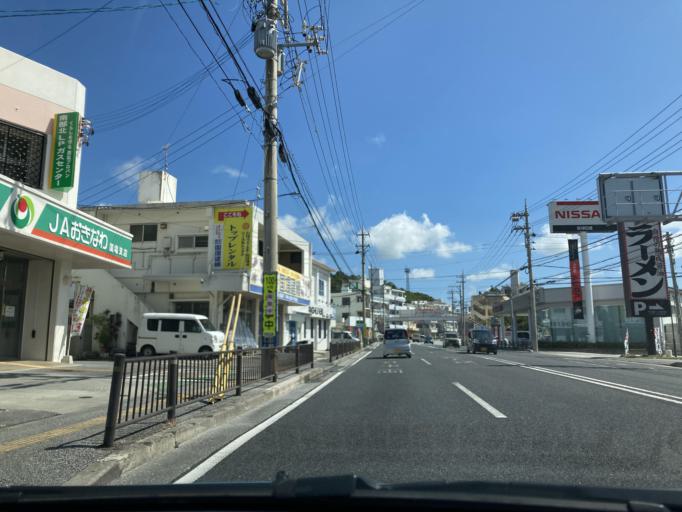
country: JP
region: Okinawa
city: Tomigusuku
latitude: 26.1966
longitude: 127.7058
